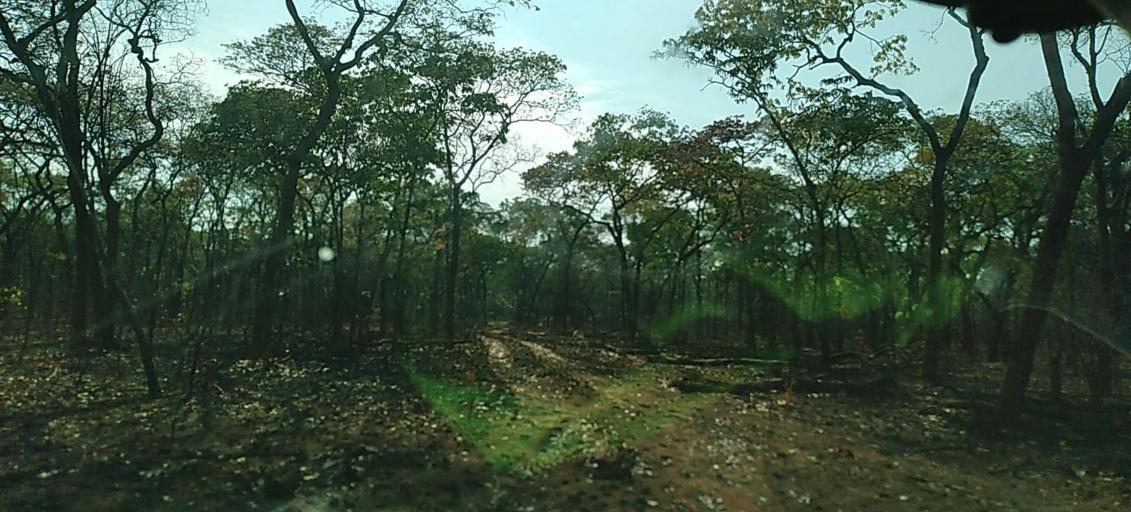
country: ZM
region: North-Western
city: Kalengwa
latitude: -13.2281
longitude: 25.0835
